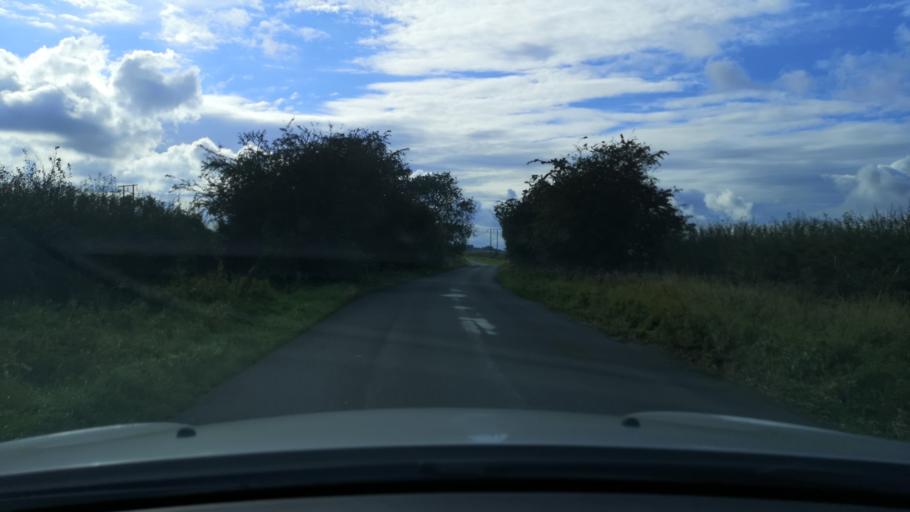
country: GB
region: England
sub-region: East Riding of Yorkshire
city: Walkington
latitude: 53.8317
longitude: -0.4963
